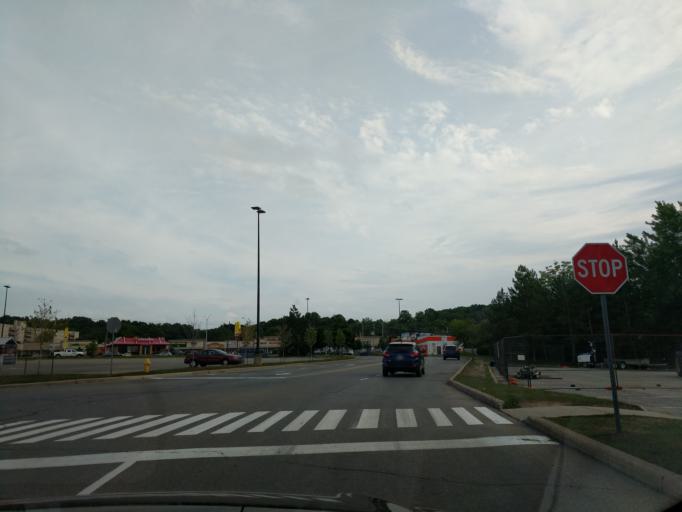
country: CA
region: Ontario
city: Thorold
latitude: 43.1339
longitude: -79.2265
